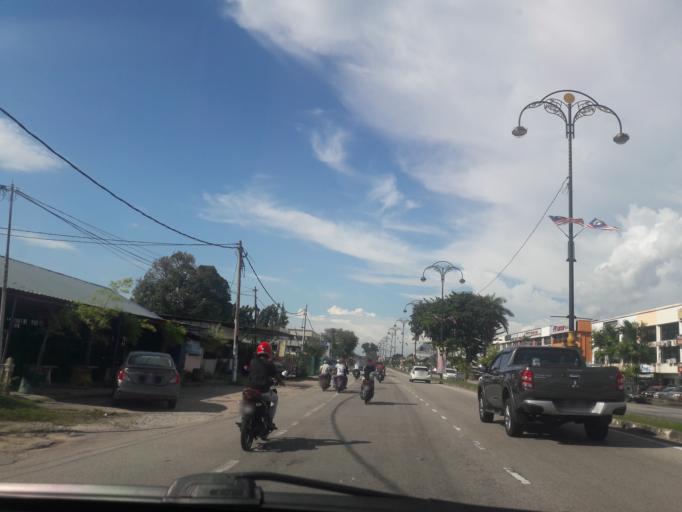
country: MY
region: Kedah
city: Sungai Petani
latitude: 5.6256
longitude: 100.4792
